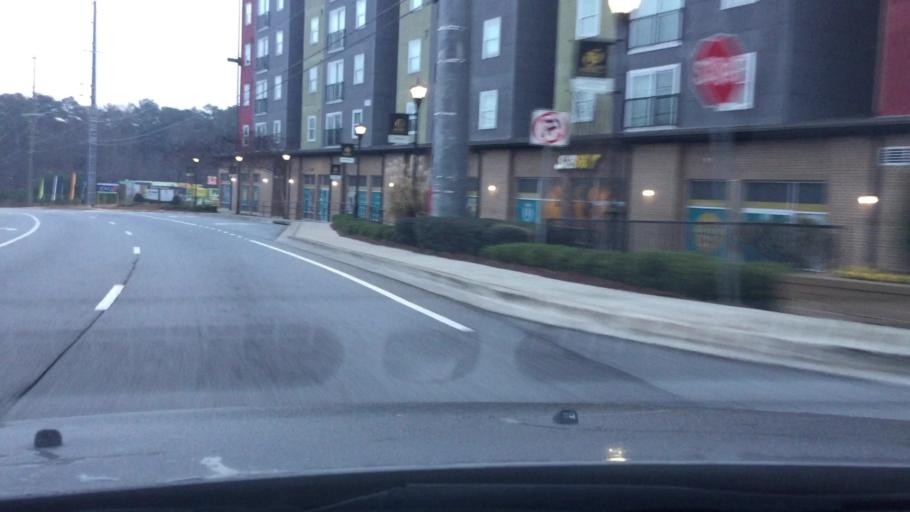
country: US
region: Georgia
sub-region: Cobb County
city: Kennesaw
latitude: 34.0277
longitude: -84.5654
